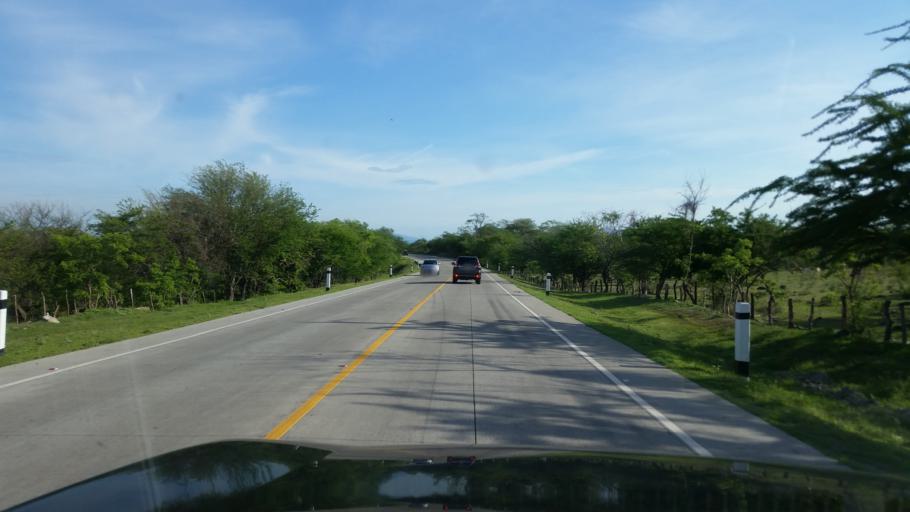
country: NI
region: Leon
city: Nagarote
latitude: 12.2067
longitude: -86.6805
